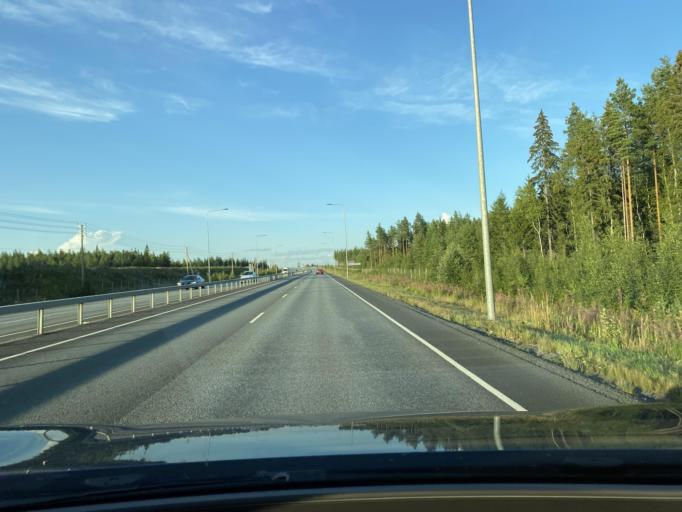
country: FI
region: Southern Ostrobothnia
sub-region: Seinaejoki
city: Nurmo
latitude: 62.7346
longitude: 22.9030
